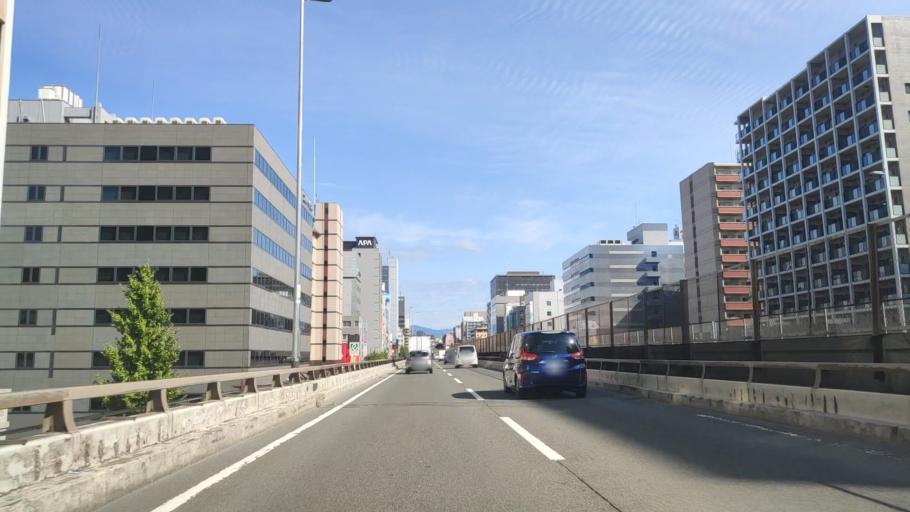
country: JP
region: Osaka
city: Suita
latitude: 34.7550
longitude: 135.4967
